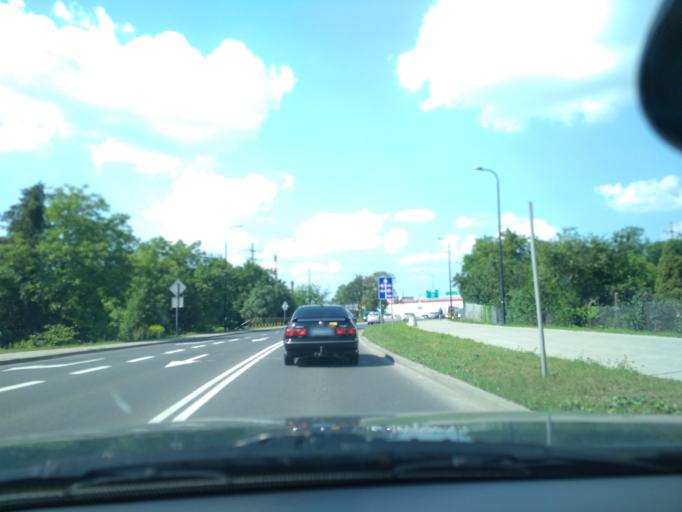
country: PL
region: Silesian Voivodeship
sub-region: Gliwice
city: Gliwice
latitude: 50.3021
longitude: 18.6591
